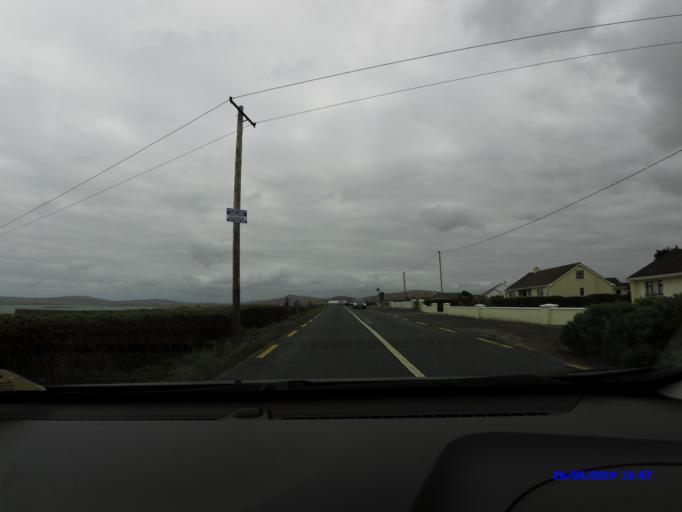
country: IE
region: Connaught
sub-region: Maigh Eo
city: Belmullet
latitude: 54.2087
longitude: -9.9384
